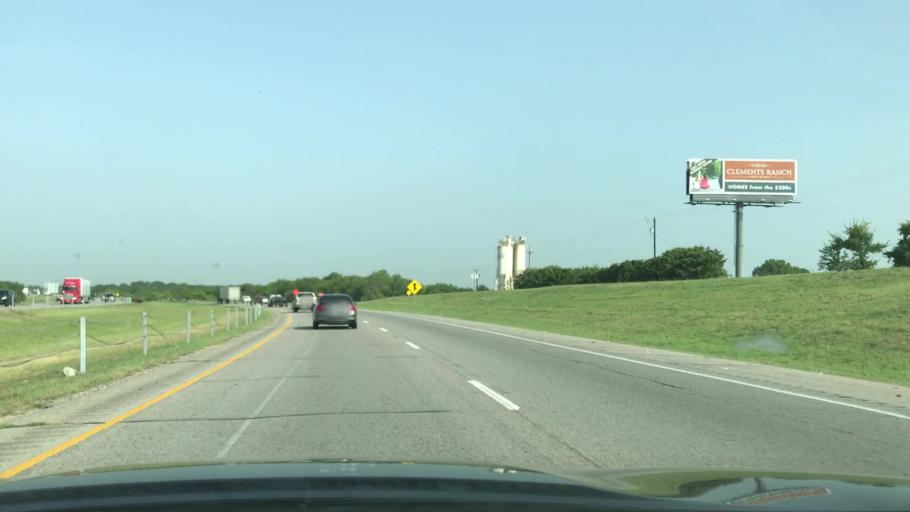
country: US
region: Texas
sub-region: Kaufman County
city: Forney
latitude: 32.7714
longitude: -96.4907
